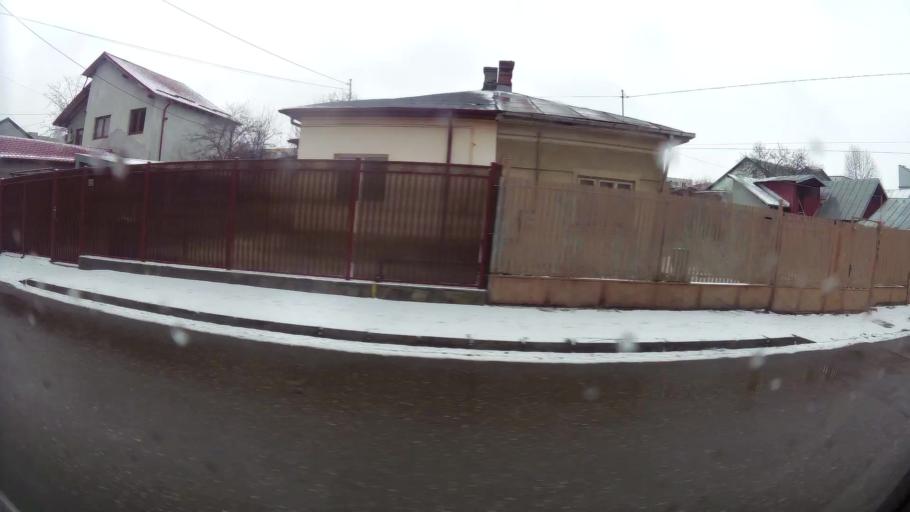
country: RO
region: Prahova
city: Ploiesti
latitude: 44.9505
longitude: 26.0103
